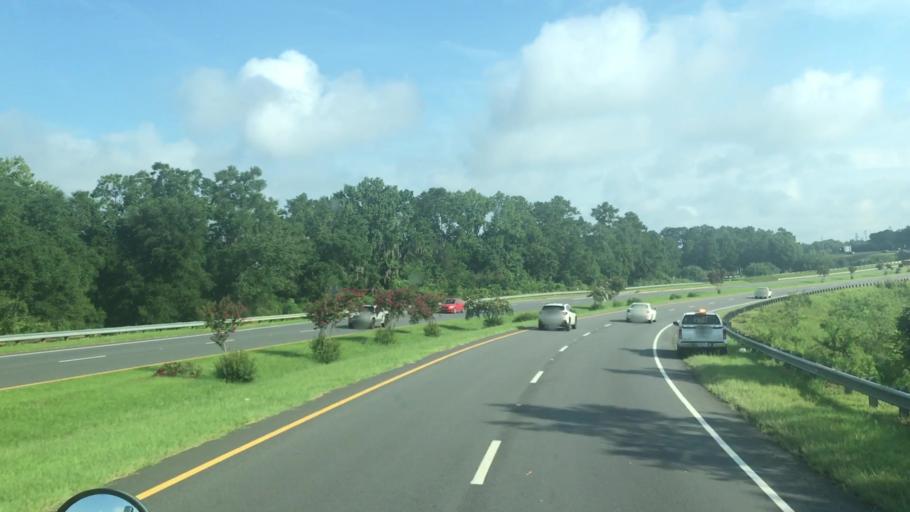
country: US
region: Georgia
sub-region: Decatur County
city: Bainbridge
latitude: 30.8993
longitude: -84.5874
